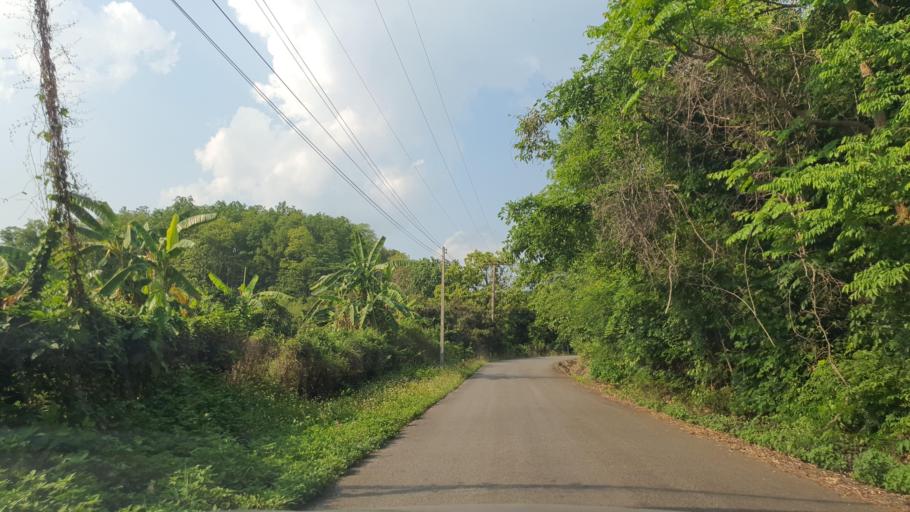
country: TH
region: Chiang Mai
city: Mae Wang
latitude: 18.6869
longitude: 98.8142
